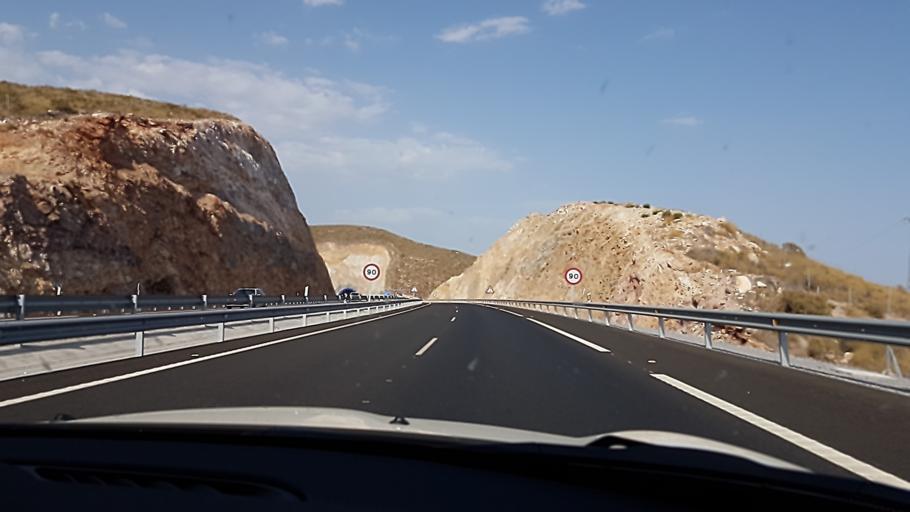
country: ES
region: Andalusia
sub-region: Provincia de Granada
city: Gualchos
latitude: 36.7172
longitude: -3.3800
